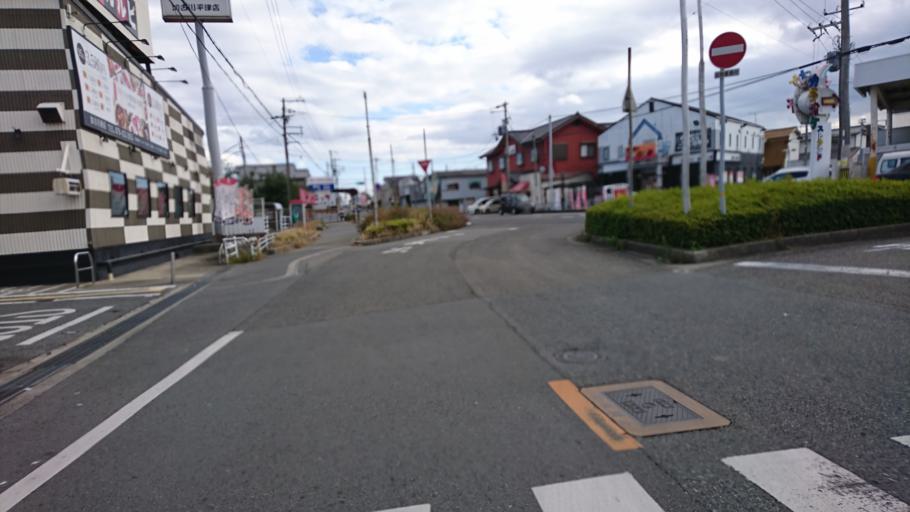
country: JP
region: Hyogo
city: Kakogawacho-honmachi
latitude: 34.7763
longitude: 134.8242
